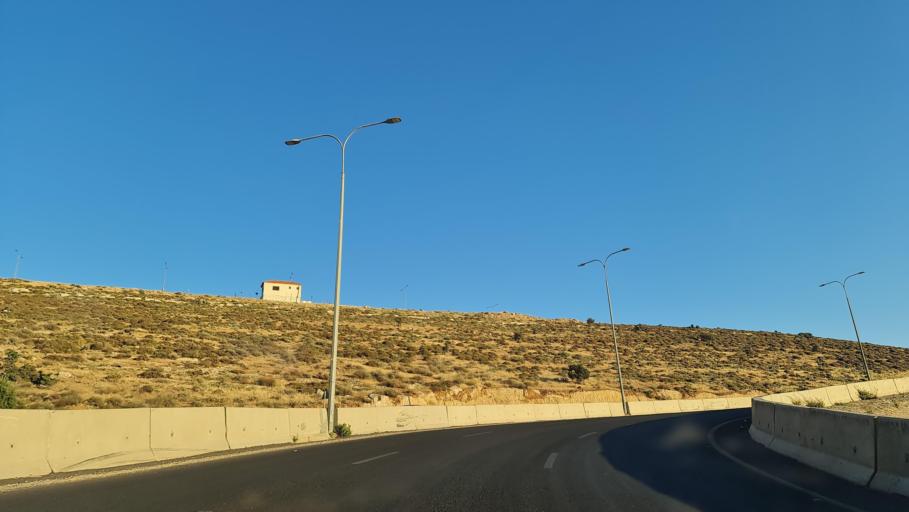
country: JO
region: Zarqa
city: Russeifa
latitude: 32.0936
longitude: 35.9619
